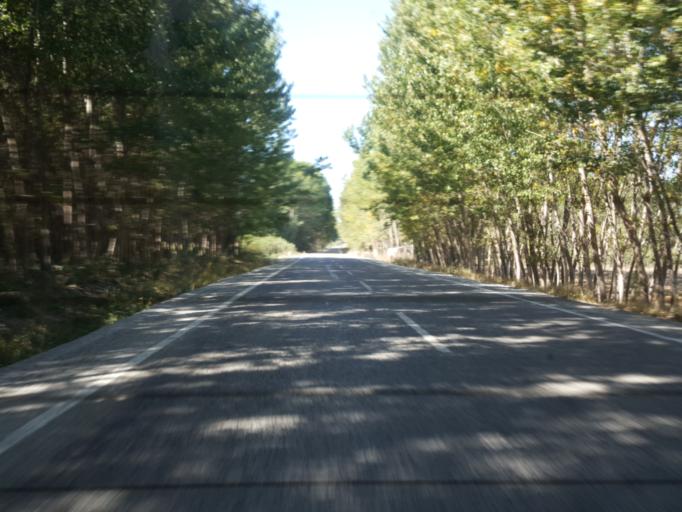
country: TR
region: Tokat
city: Pazar
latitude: 40.2683
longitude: 36.2099
